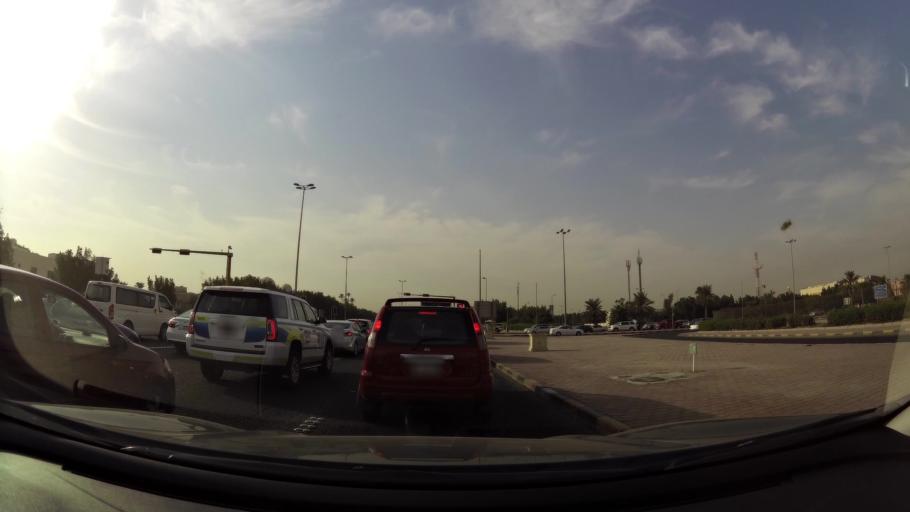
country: KW
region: Muhafazat Hawalli
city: Ar Rumaythiyah
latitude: 29.3089
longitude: 48.0861
